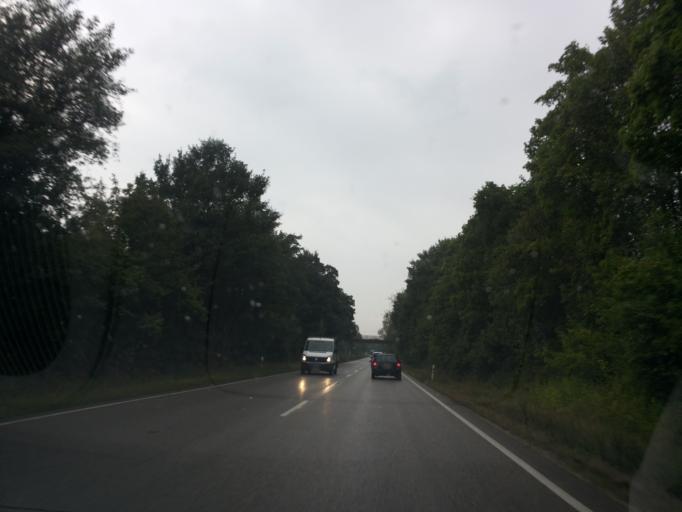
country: DE
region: Bavaria
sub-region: Upper Bavaria
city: Lenting
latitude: 48.7759
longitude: 11.4892
